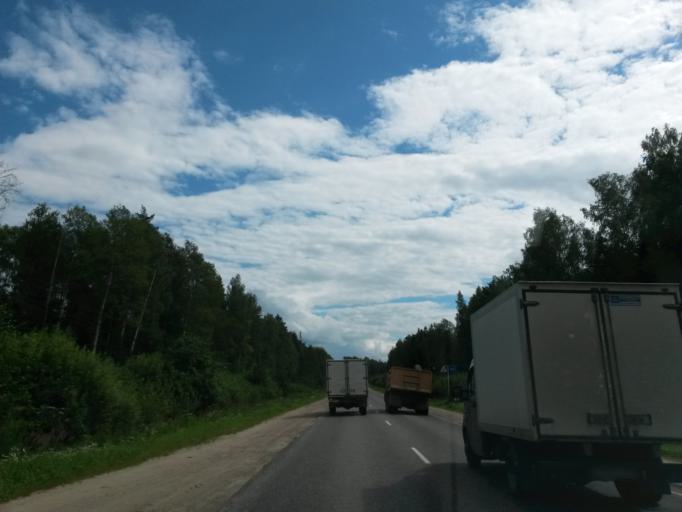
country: RU
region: Ivanovo
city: Novo-Talitsy
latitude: 57.0566
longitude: 40.7278
